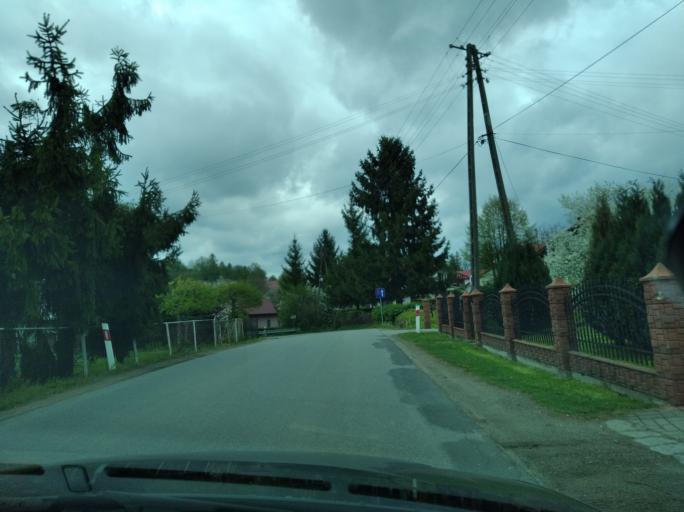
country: PL
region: Subcarpathian Voivodeship
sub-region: Powiat sanocki
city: Dlugie
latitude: 49.6037
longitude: 22.0531
